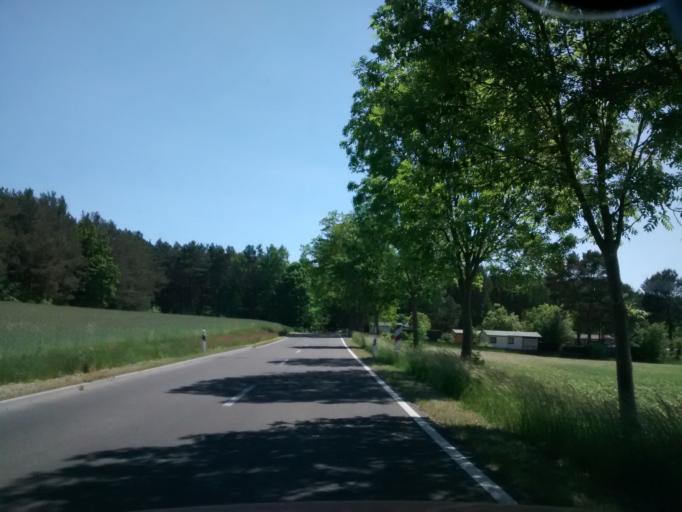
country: DE
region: Brandenburg
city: Reichenwalde
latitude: 52.2344
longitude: 13.9947
